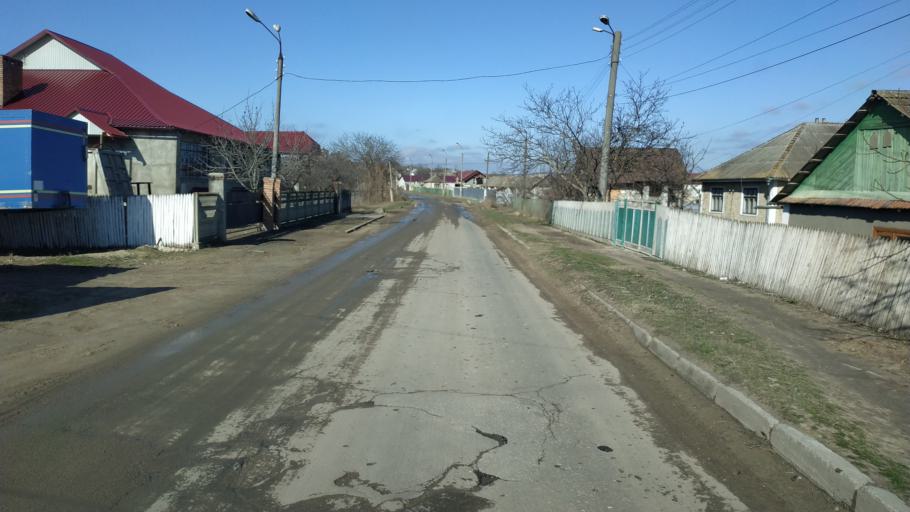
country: MD
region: Hincesti
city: Hincesti
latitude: 46.9702
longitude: 28.5881
